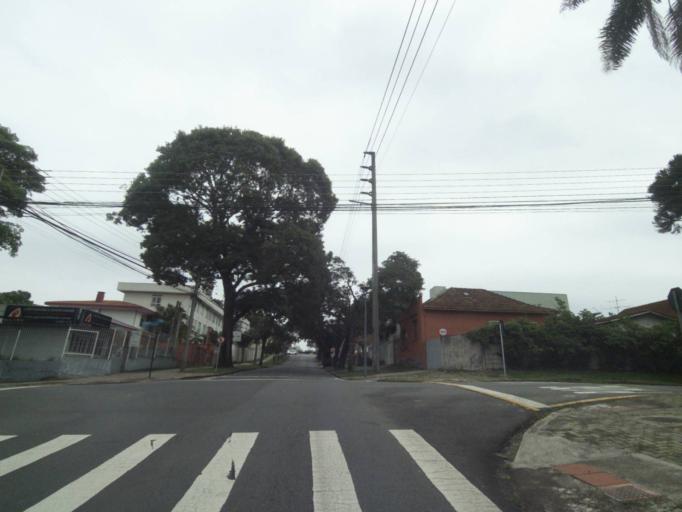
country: BR
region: Parana
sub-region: Curitiba
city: Curitiba
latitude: -25.4201
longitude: -49.2885
